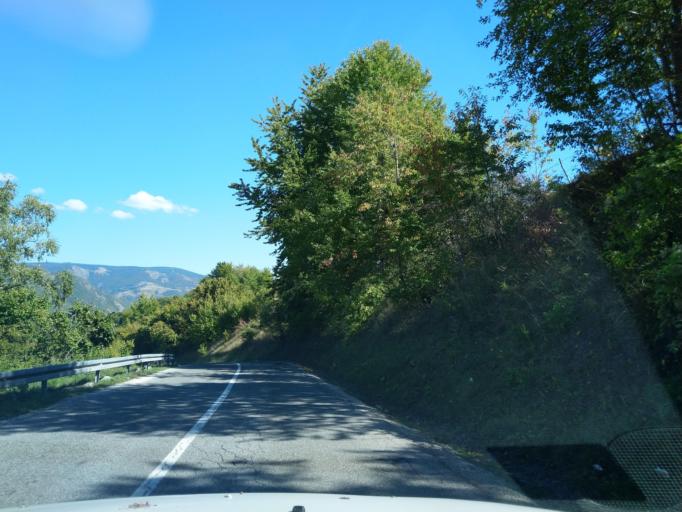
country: RS
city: Sokolovica
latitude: 43.2481
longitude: 20.2352
